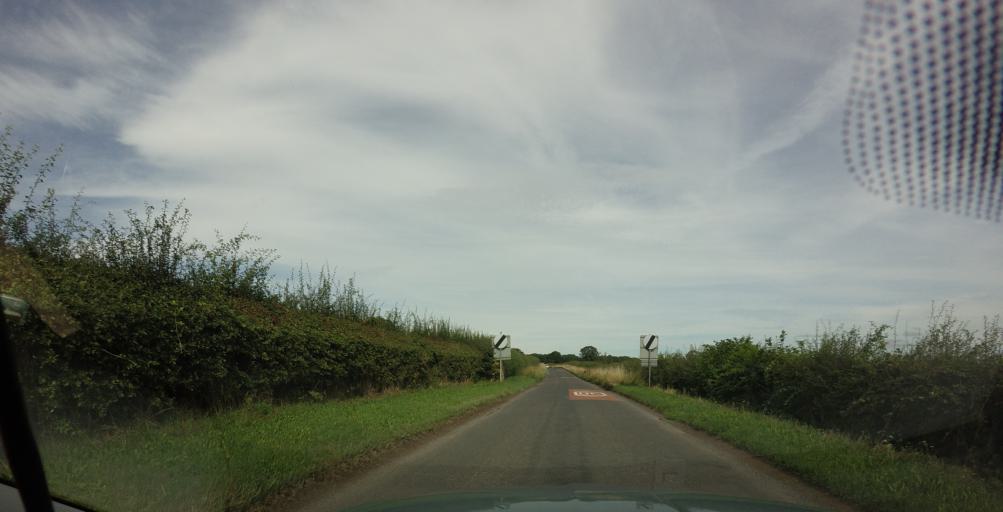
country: GB
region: England
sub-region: North Yorkshire
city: Ripon
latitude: 54.0938
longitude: -1.5063
